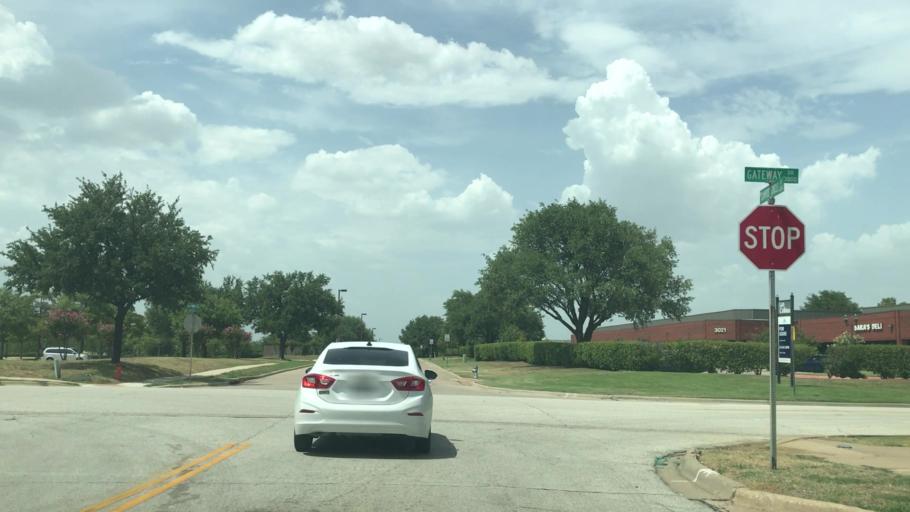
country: US
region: Texas
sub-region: Dallas County
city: Coppell
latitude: 32.8937
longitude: -96.9893
